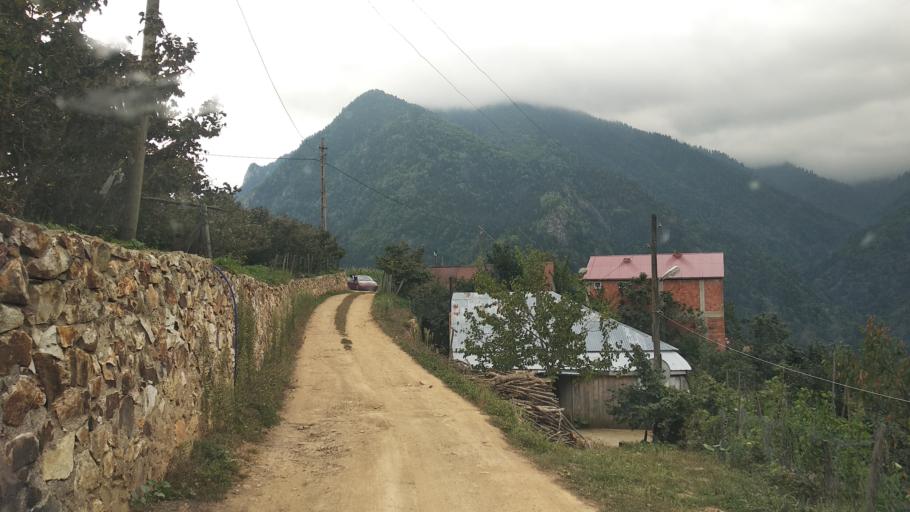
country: TR
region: Giresun
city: Dogankent
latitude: 40.7425
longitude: 38.9963
